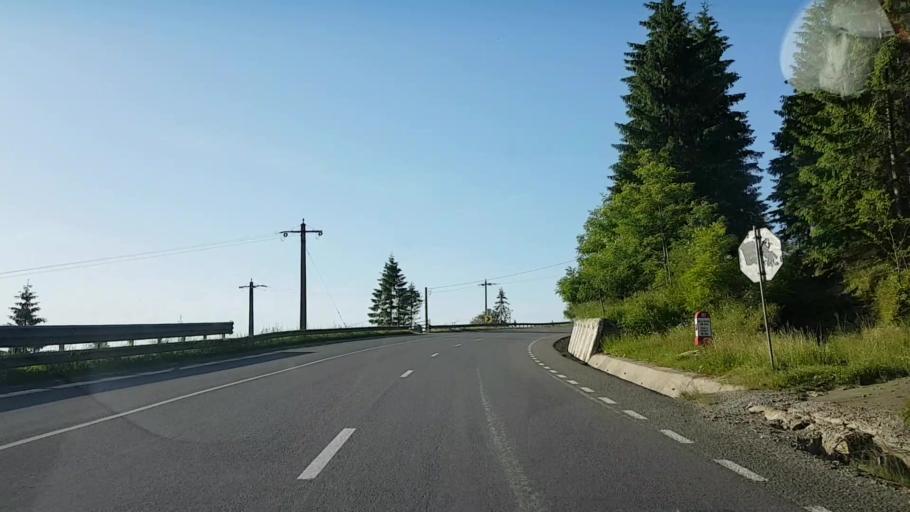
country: RO
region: Bistrita-Nasaud
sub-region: Comuna Lunca Ilvei
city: Lunca Ilvei
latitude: 47.2419
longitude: 25.0191
